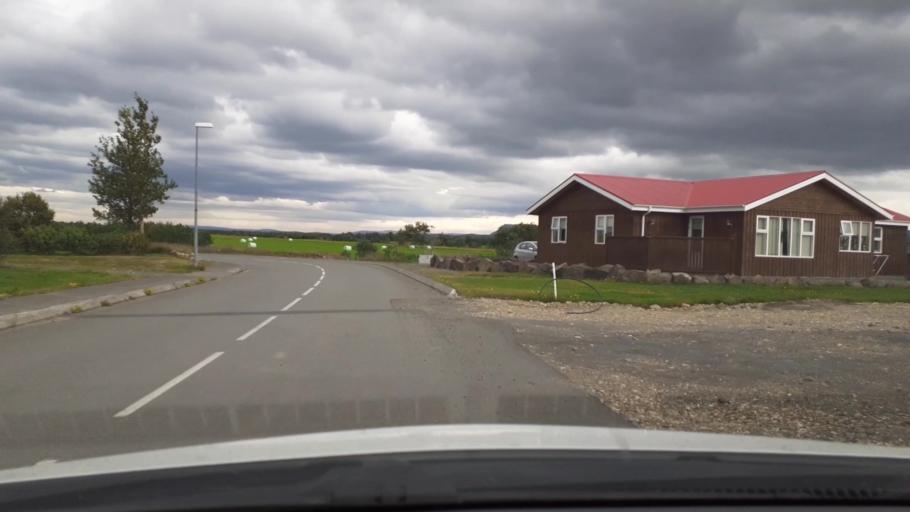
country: IS
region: West
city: Borgarnes
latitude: 64.5611
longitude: -21.7566
